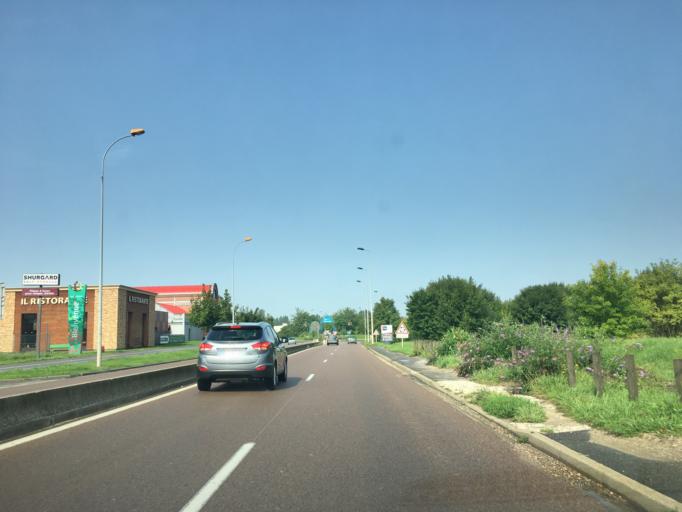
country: FR
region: Ile-de-France
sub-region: Departement du Val-de-Marne
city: La Queue-en-Brie
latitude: 48.7783
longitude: 2.5885
